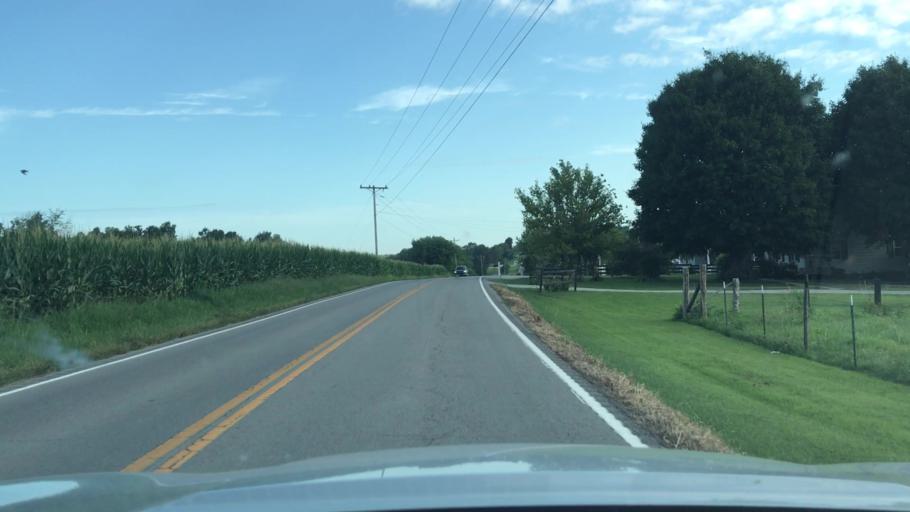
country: US
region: Kentucky
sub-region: Todd County
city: Elkton
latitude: 36.8763
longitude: -87.1668
